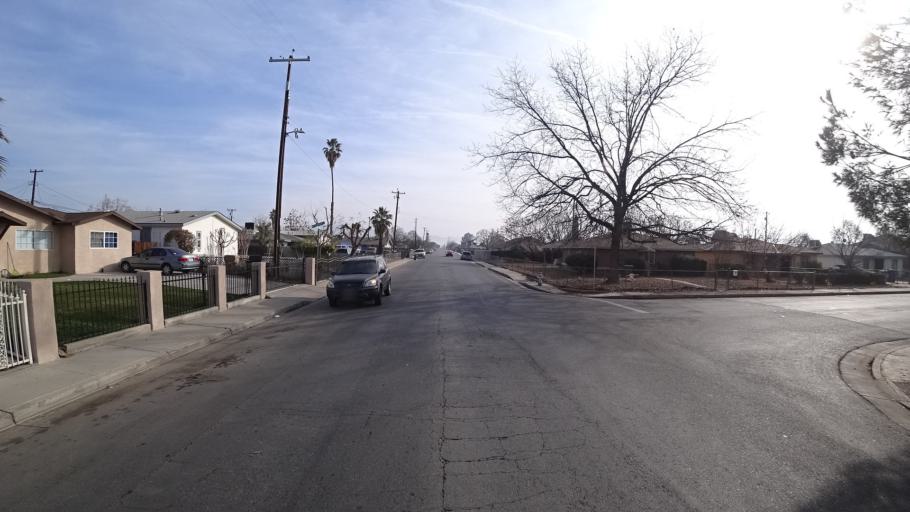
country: US
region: California
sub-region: Kern County
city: Bakersfield
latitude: 35.3612
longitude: -118.9898
